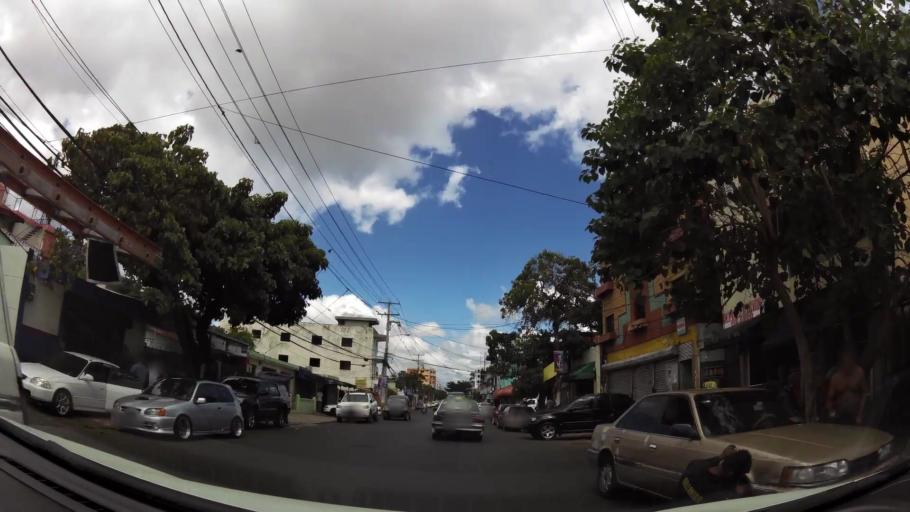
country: DO
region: Nacional
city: Ensanche Luperon
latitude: 18.5024
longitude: -69.8950
